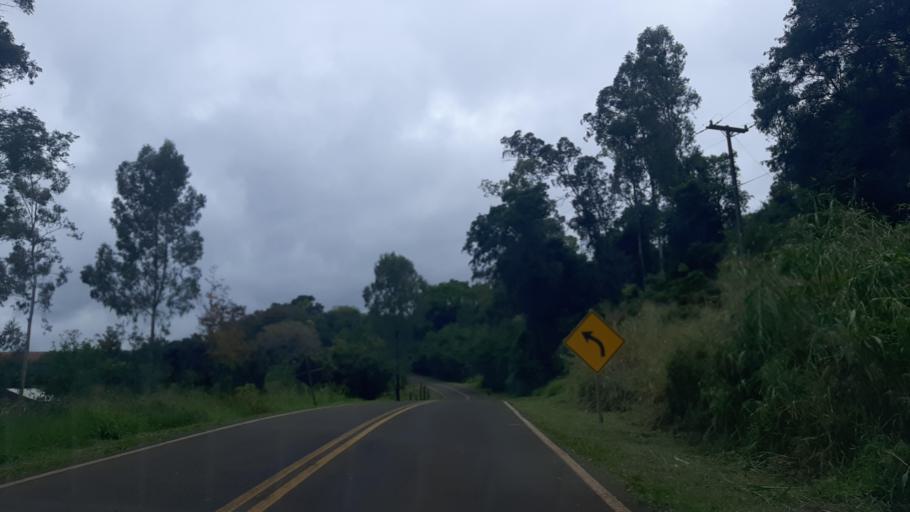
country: BR
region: Parana
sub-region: Ampere
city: Ampere
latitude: -25.9388
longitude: -53.4629
